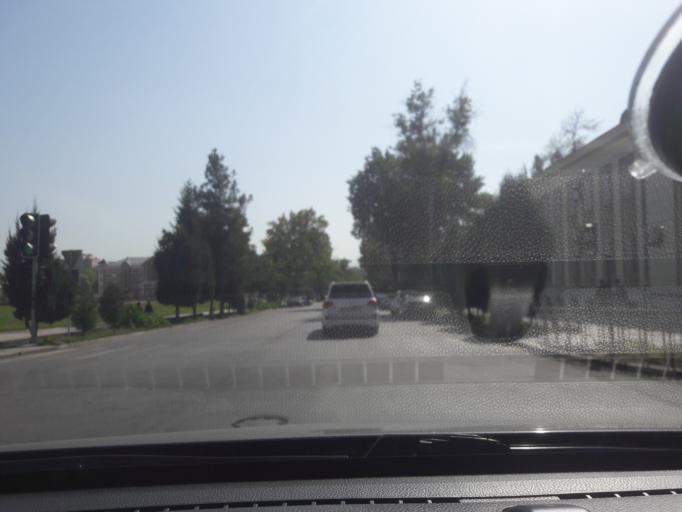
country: TJ
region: Dushanbe
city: Dushanbe
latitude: 38.5677
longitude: 68.7998
